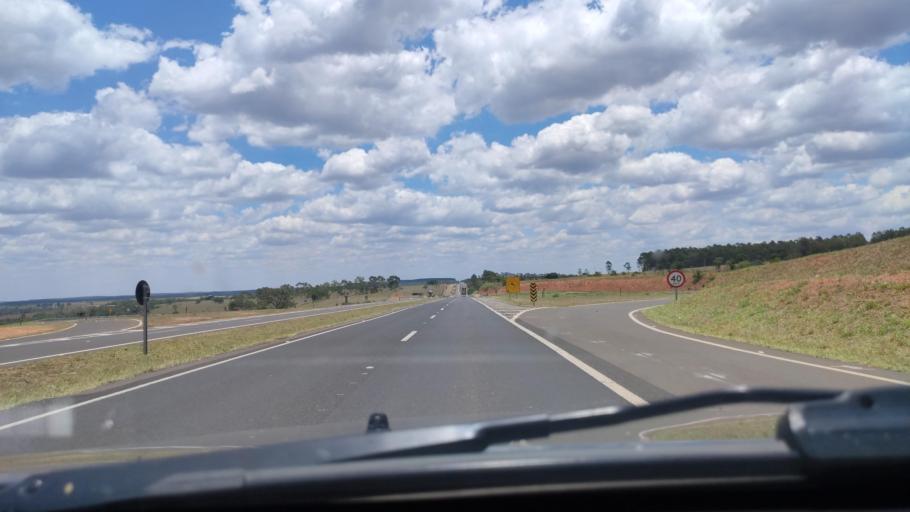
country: BR
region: Sao Paulo
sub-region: Duartina
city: Duartina
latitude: -22.4953
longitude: -49.2620
